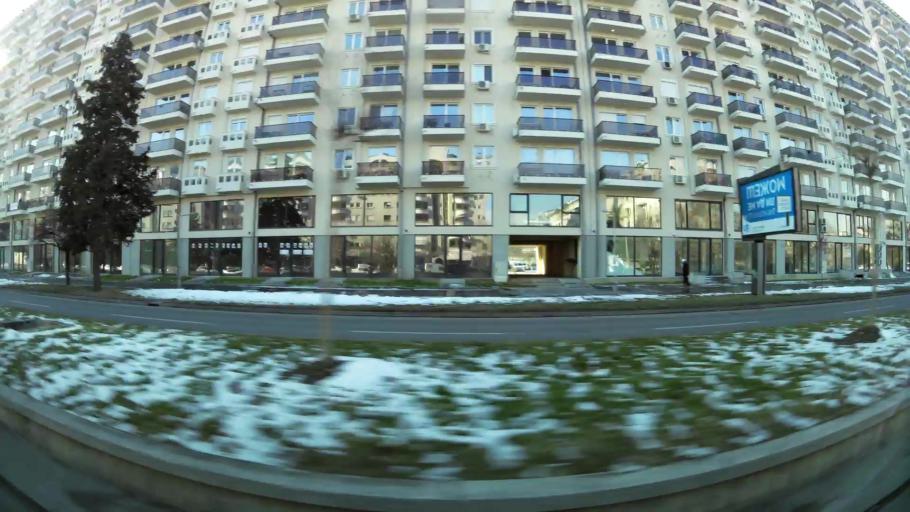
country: MK
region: Karpos
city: Skopje
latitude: 41.9991
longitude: 21.4041
